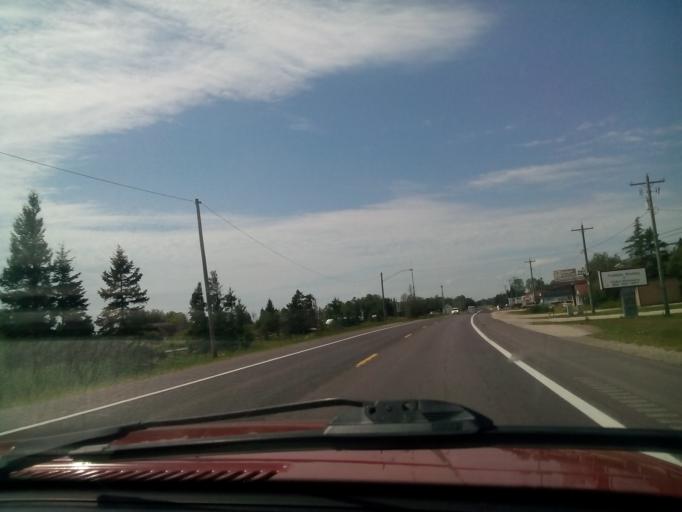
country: US
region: Michigan
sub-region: Schoolcraft County
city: Manistique
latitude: 45.9926
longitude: -86.0139
